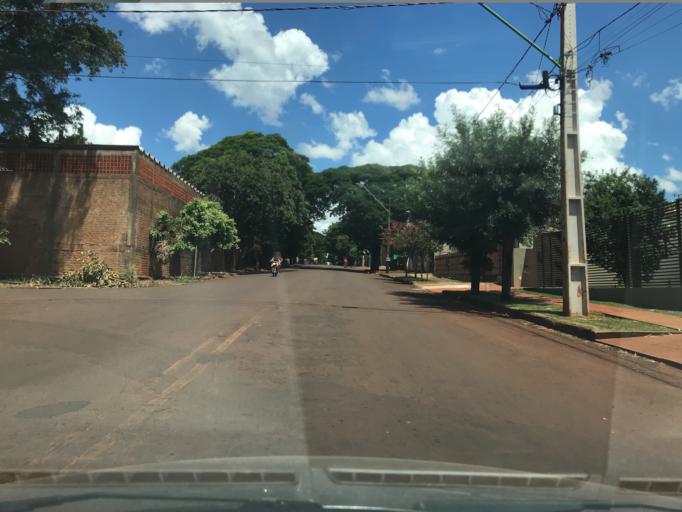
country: BR
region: Parana
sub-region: Palotina
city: Palotina
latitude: -24.2814
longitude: -53.8480
